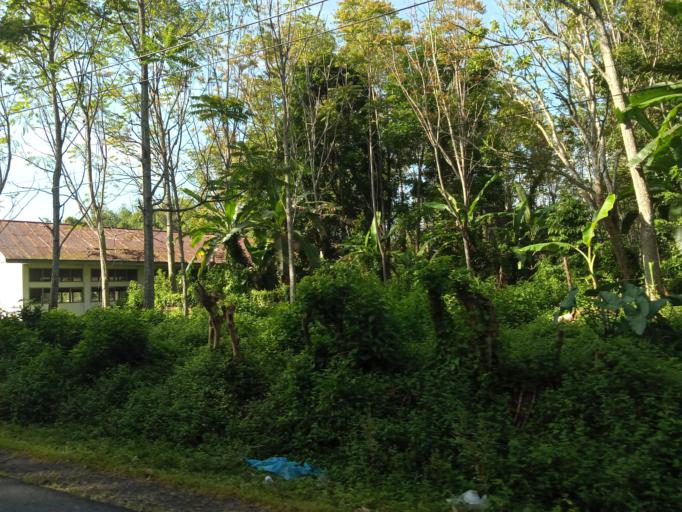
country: ID
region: Jambi
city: Sungai Penuh
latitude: -2.0976
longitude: 101.4606
